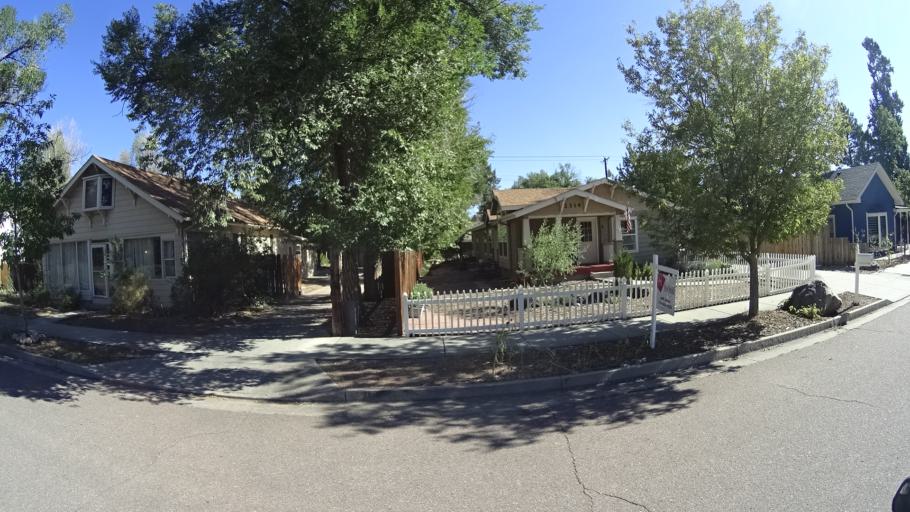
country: US
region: Colorado
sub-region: El Paso County
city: Colorado Springs
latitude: 38.8445
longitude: -104.8619
